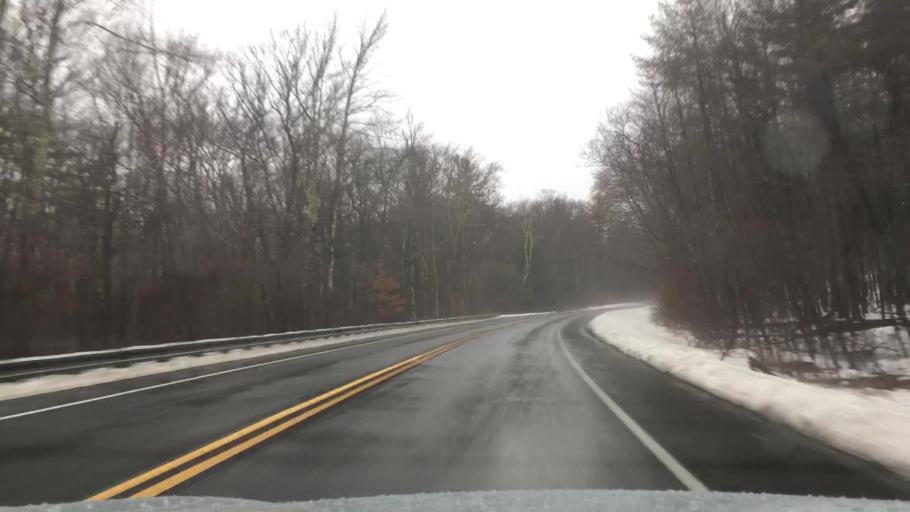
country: US
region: Massachusetts
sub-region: Hampshire County
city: Pelham
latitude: 42.4116
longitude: -72.4022
